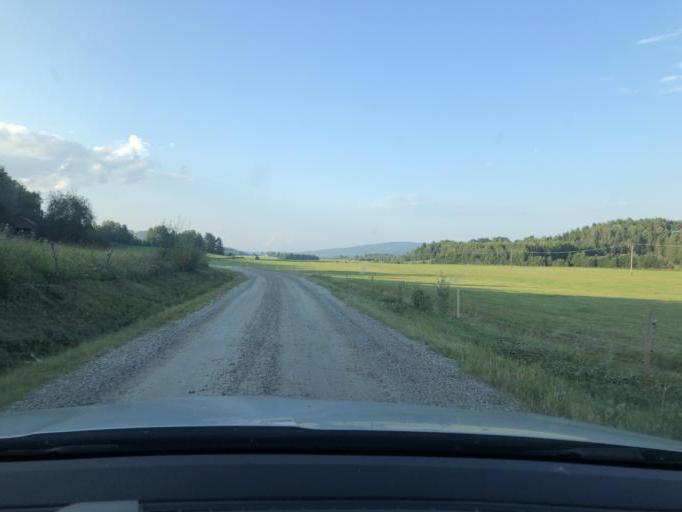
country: SE
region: Vaesternorrland
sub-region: Kramfors Kommun
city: Bollstabruk
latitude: 63.0600
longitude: 17.7329
